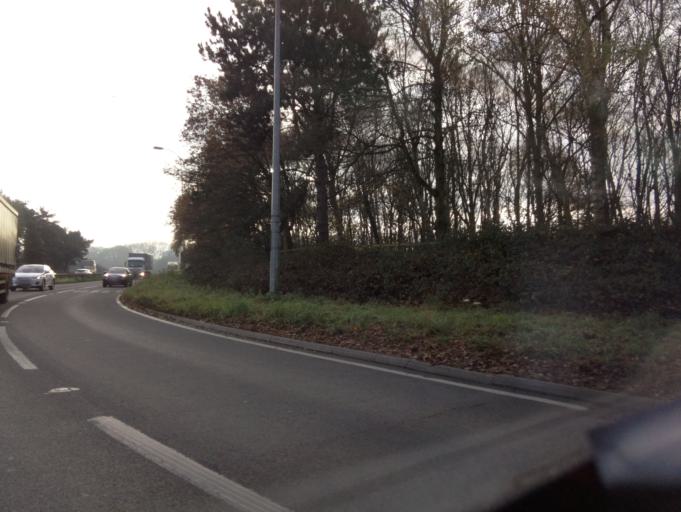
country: GB
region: England
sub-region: Staffordshire
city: Lichfield
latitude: 52.6620
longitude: -1.8144
